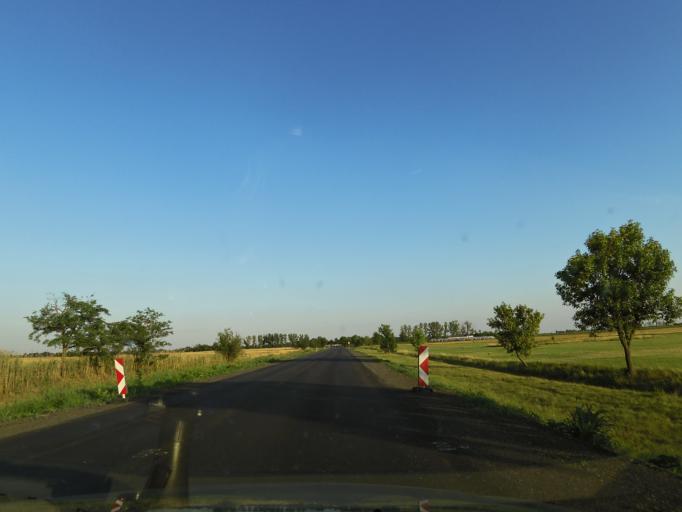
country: HU
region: Csongrad
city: Szentes
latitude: 46.6120
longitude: 20.2882
